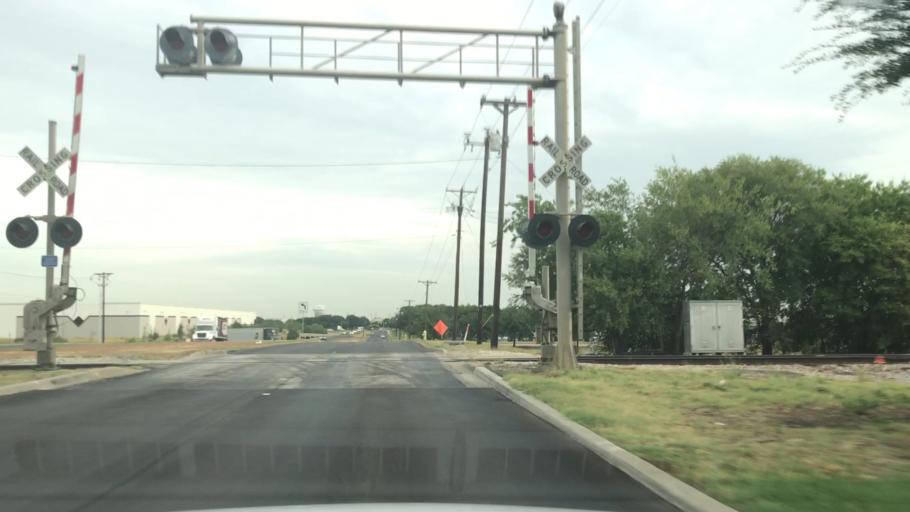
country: US
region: Texas
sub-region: Dallas County
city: Coppell
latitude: 32.9487
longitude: -97.0221
